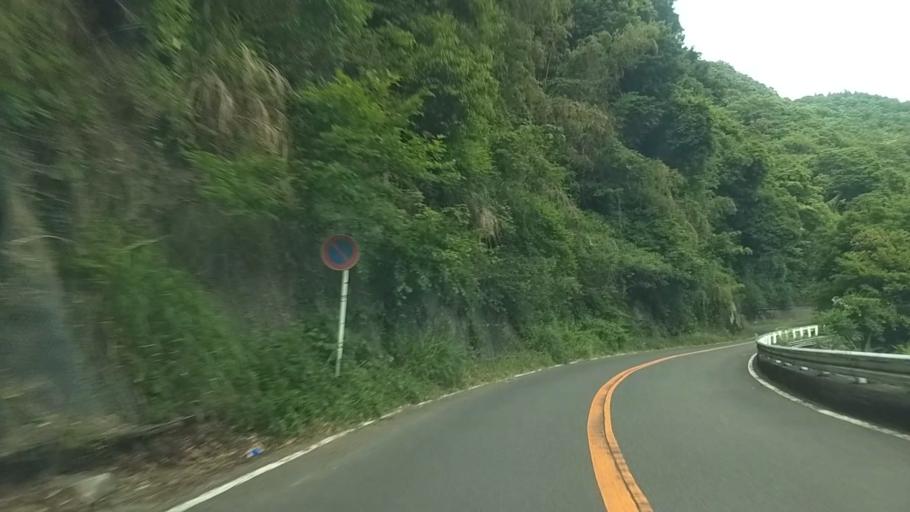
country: JP
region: Shizuoka
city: Gotemba
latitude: 35.3646
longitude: 139.0530
